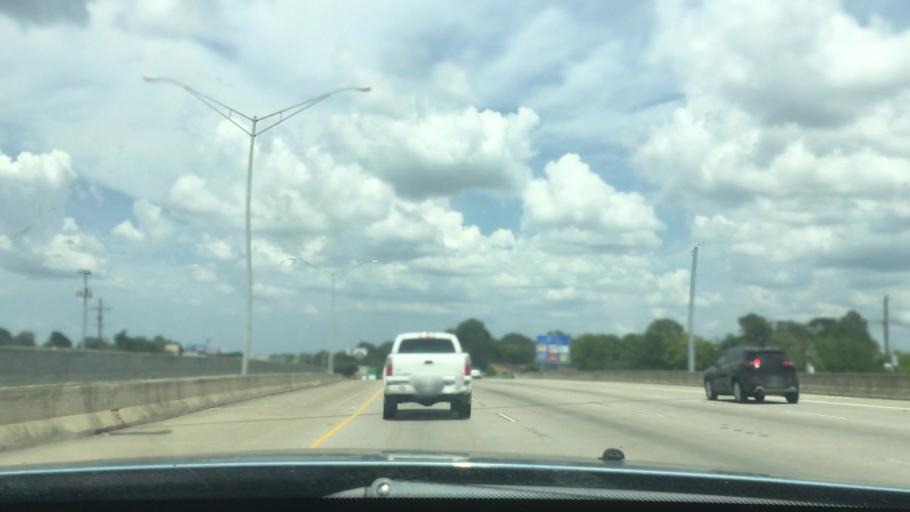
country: US
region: Louisiana
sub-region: East Baton Rouge Parish
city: Westminster
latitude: 30.4175
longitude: -91.0903
